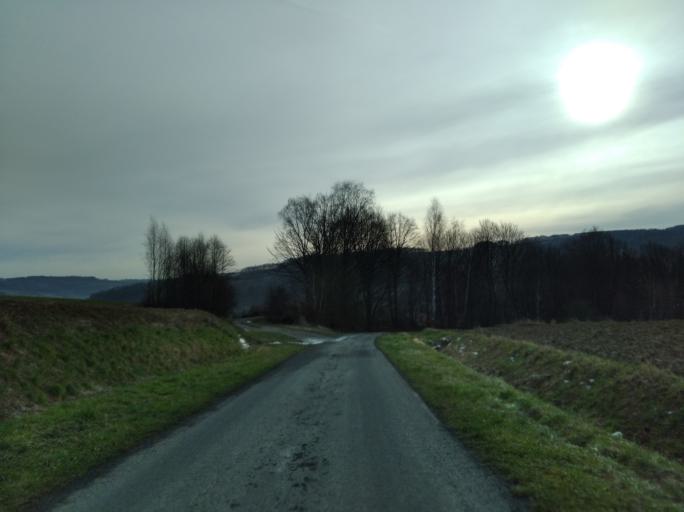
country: PL
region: Subcarpathian Voivodeship
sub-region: Powiat strzyzowski
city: Czudec
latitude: 49.9274
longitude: 21.7993
